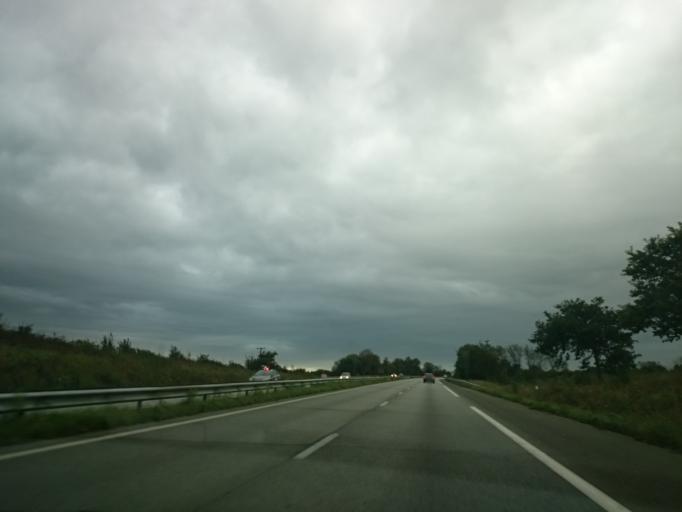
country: FR
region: Brittany
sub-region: Departement du Finistere
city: Landrevarzec
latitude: 48.0578
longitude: -4.0540
